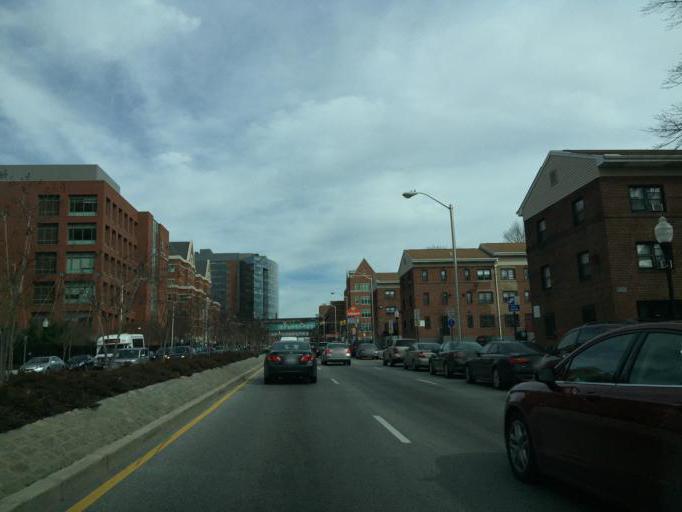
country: US
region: Maryland
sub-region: City of Baltimore
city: Baltimore
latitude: 39.2951
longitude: -76.5959
